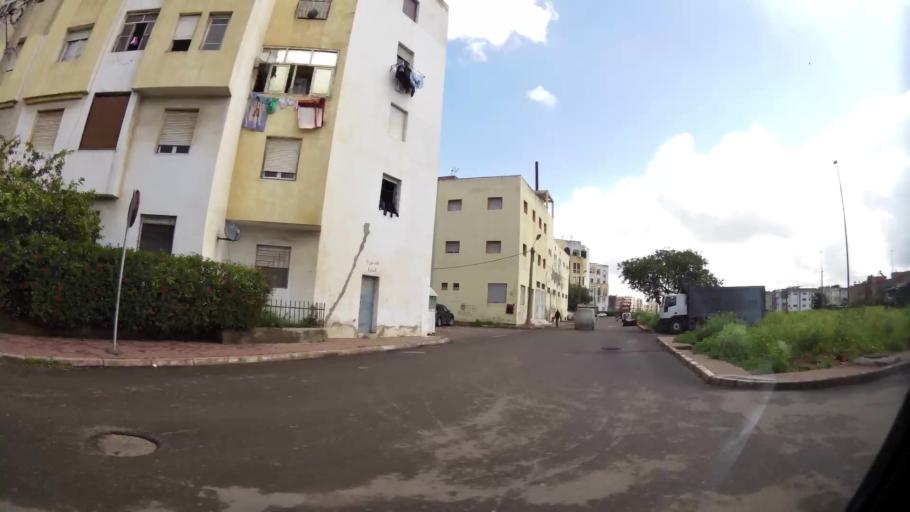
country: MA
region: Grand Casablanca
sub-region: Mediouna
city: Tit Mellil
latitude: 33.5527
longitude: -7.4811
